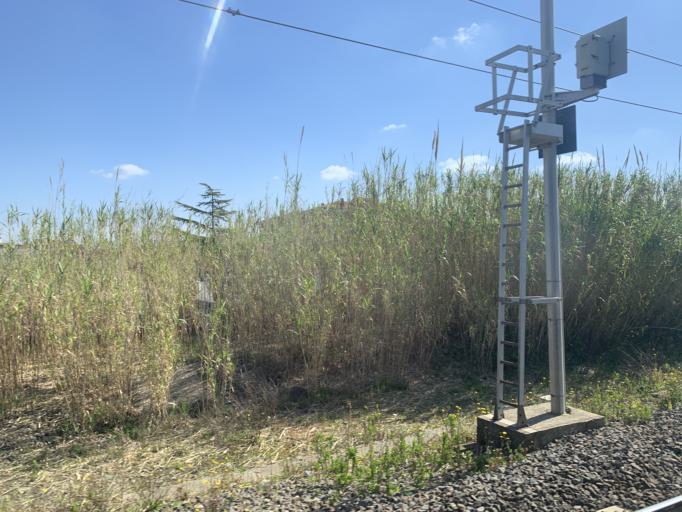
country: IT
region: Latium
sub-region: Citta metropolitana di Roma Capitale
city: Ciampino
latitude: 41.8081
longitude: 12.5922
